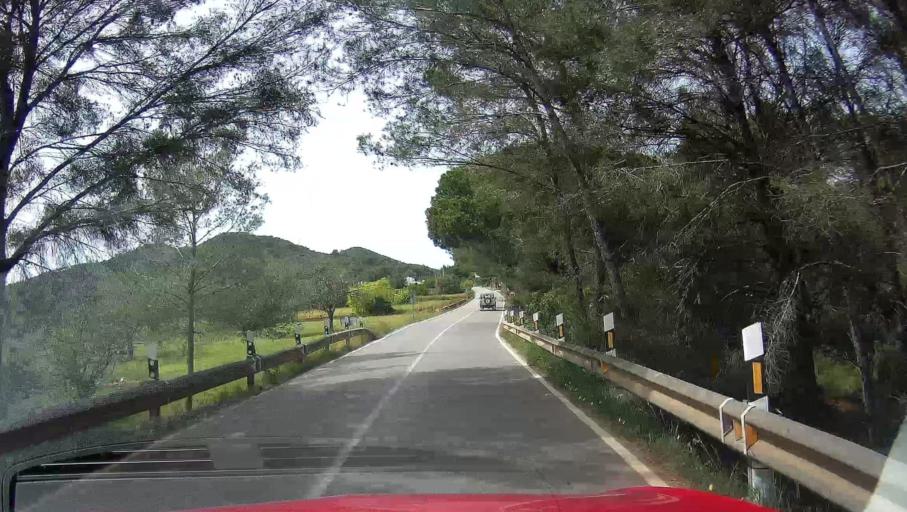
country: ES
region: Balearic Islands
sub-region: Illes Balears
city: Santa Eularia des Riu
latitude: 38.9874
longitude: 1.4896
